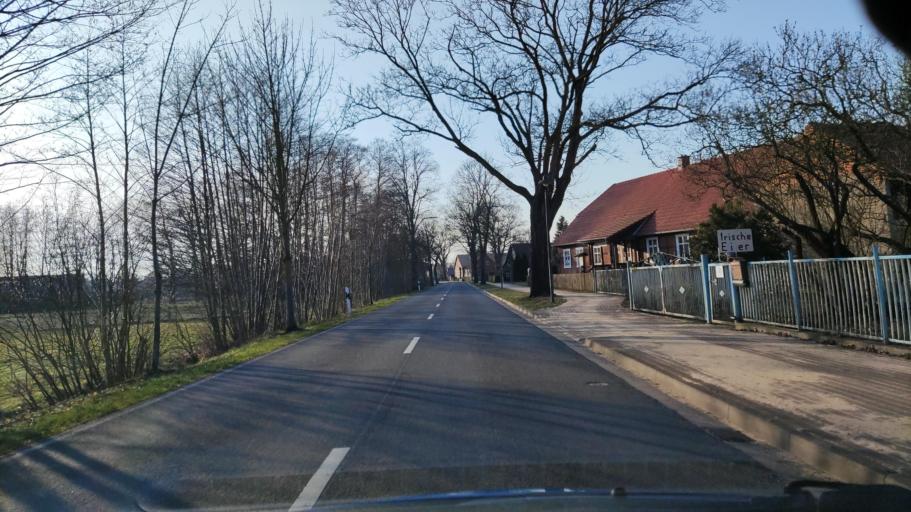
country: DE
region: Brandenburg
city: Lanz
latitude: 52.9919
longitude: 11.5842
